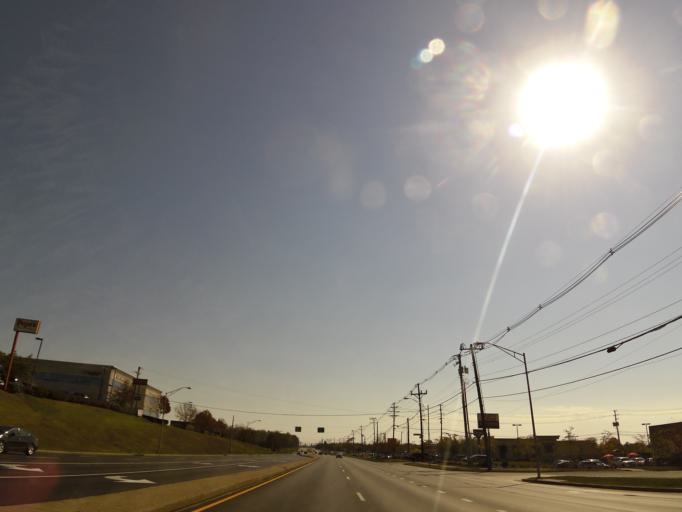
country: US
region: Kentucky
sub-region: Fayette County
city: Lexington
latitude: 38.0003
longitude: -84.4452
